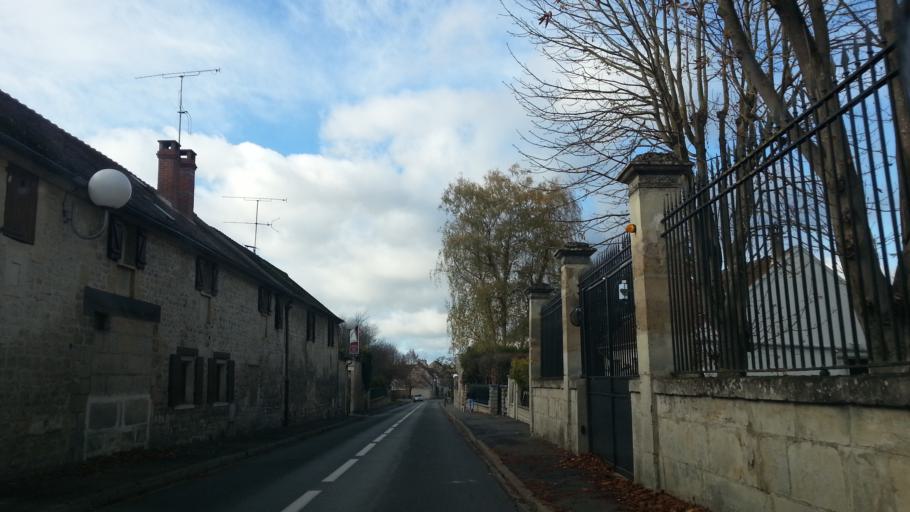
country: FR
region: Picardie
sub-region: Departement de l'Oise
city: Gouvieux
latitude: 49.1879
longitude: 2.4219
